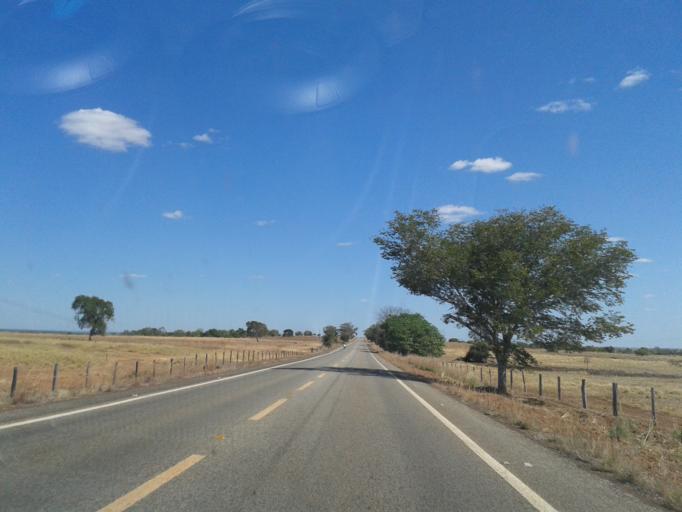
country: BR
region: Goias
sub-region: Sao Miguel Do Araguaia
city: Sao Miguel do Araguaia
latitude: -13.4070
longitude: -50.2631
